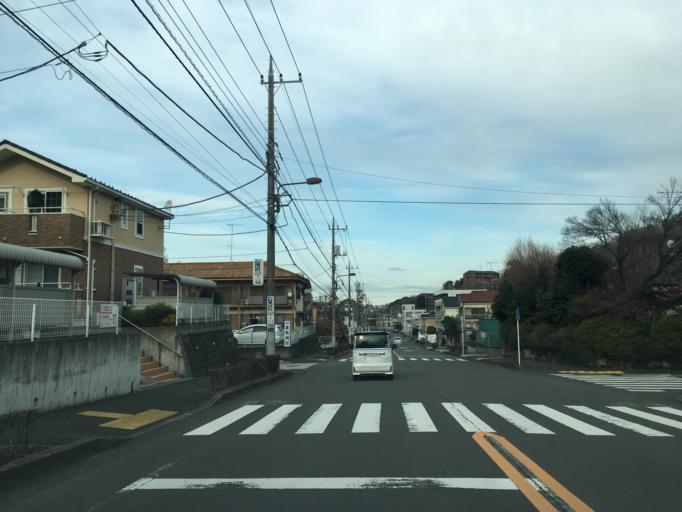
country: JP
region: Tokyo
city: Hino
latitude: 35.6258
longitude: 139.4374
